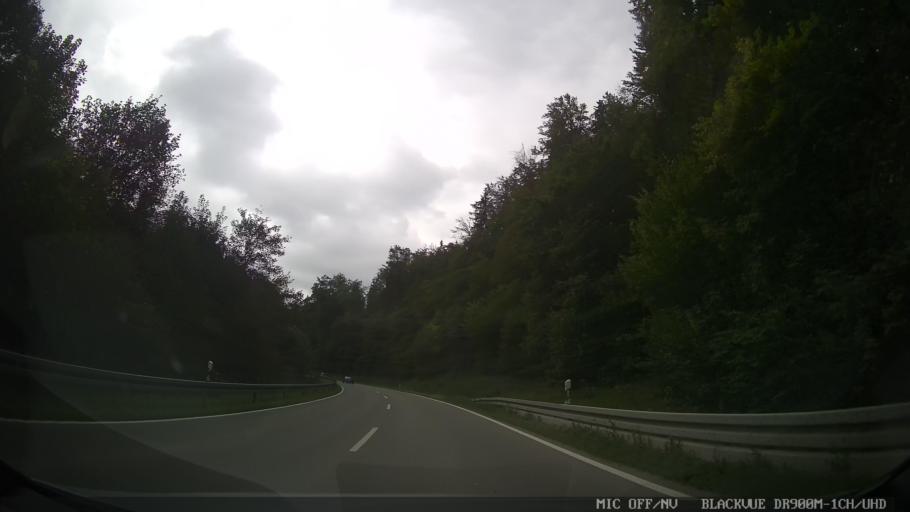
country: DE
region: Baden-Wuerttemberg
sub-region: Freiburg Region
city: Neuhausen ob Eck
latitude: 47.9882
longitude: 8.9294
